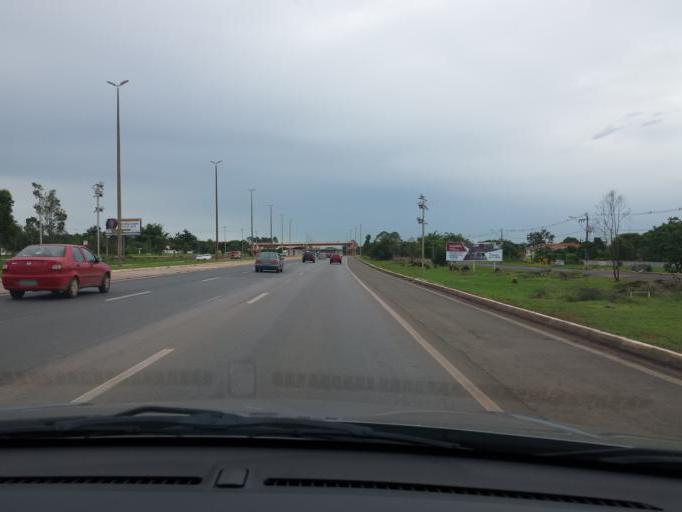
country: BR
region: Federal District
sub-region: Brasilia
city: Brasilia
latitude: -15.9140
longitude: -47.9693
